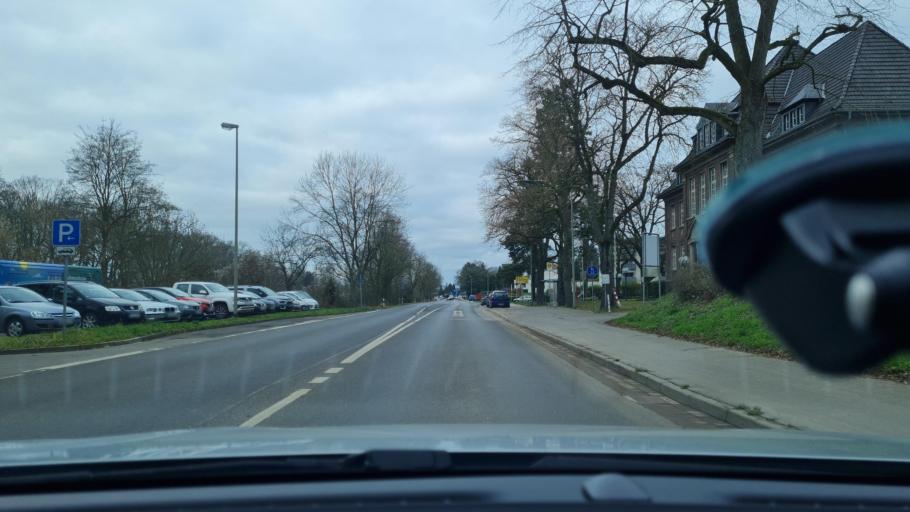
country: DE
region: North Rhine-Westphalia
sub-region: Regierungsbezirk Dusseldorf
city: Voerde
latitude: 51.5951
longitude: 6.6678
